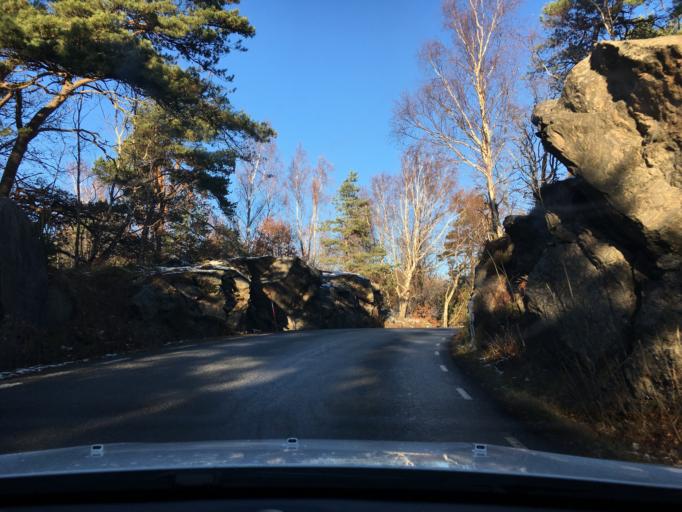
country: SE
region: Vaestra Goetaland
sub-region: Tjorns Kommun
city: Myggenas
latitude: 58.0611
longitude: 11.6818
